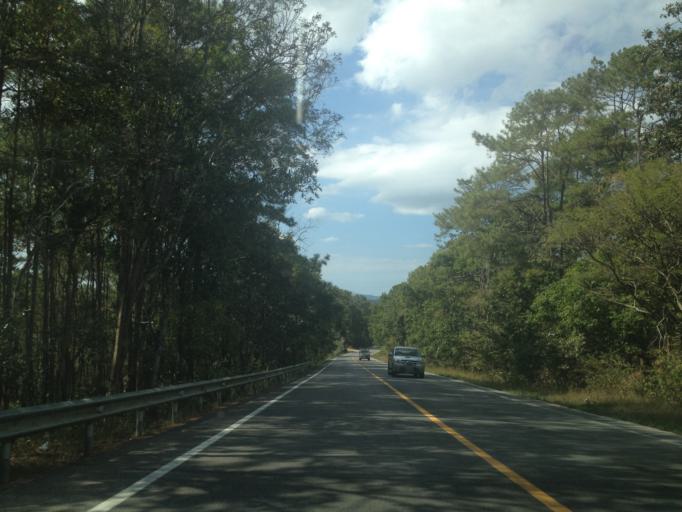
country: TH
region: Mae Hong Son
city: Pa Pae
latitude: 18.1485
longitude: 98.3063
